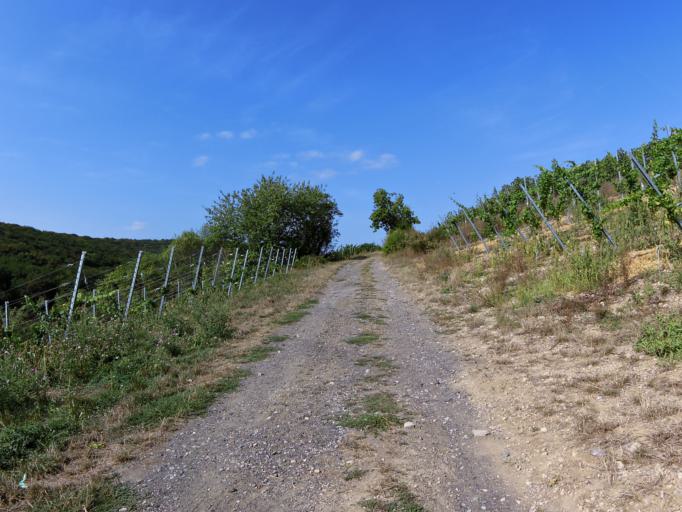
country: DE
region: Bavaria
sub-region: Regierungsbezirk Unterfranken
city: Theilheim
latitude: 49.7545
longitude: 10.0102
